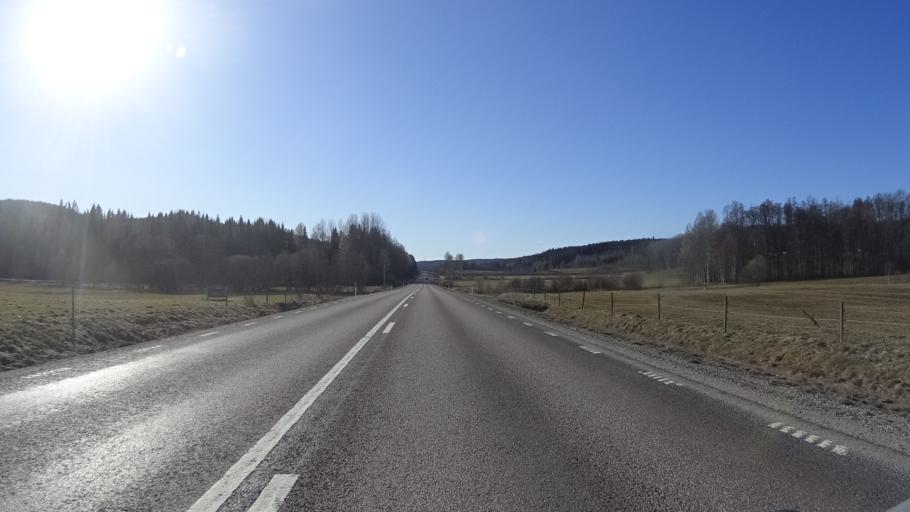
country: SE
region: Vaermland
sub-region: Arvika Kommun
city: Arvika
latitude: 59.6674
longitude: 12.8384
